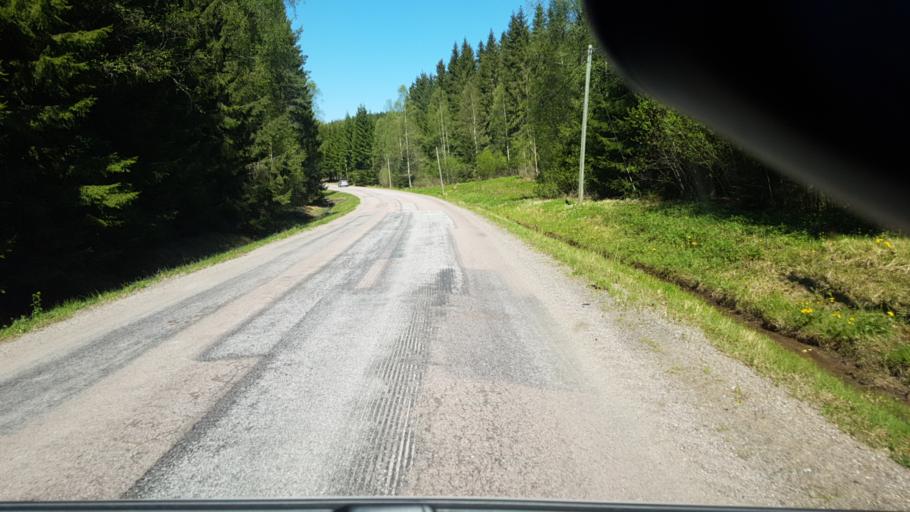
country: SE
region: Vaermland
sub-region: Eda Kommun
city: Amotfors
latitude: 59.9079
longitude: 12.5237
